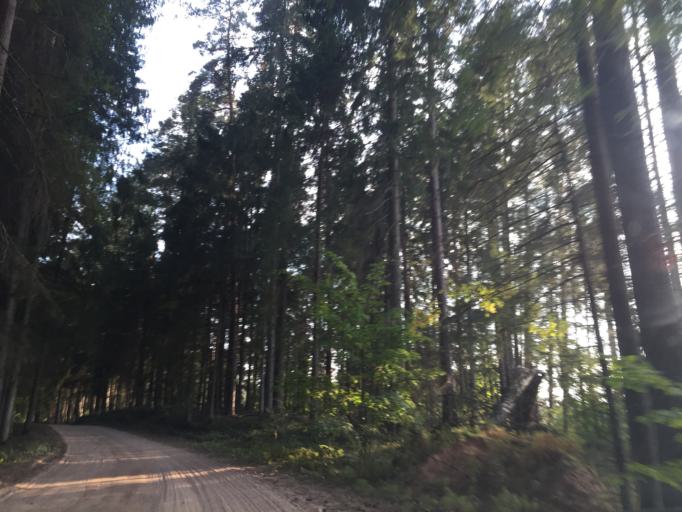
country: LV
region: Baldone
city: Baldone
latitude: 56.7600
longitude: 24.4094
